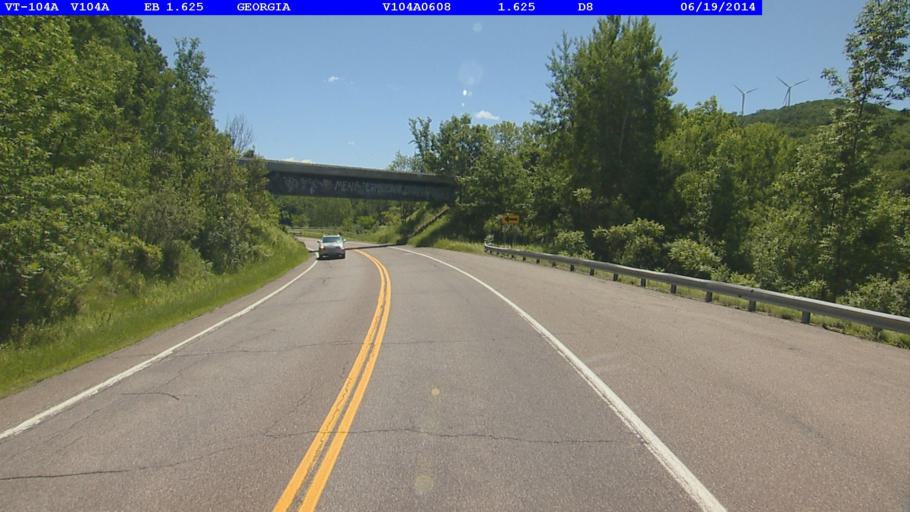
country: US
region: Vermont
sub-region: Chittenden County
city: Milton
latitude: 44.6805
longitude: -73.0840
